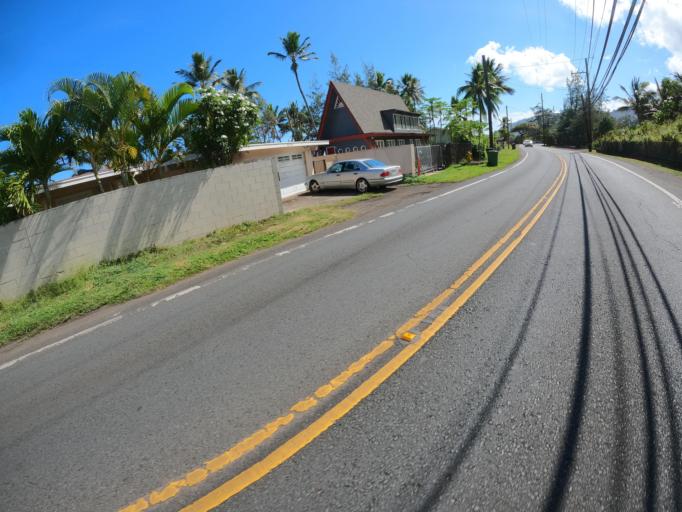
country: US
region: Hawaii
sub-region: Honolulu County
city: Hau'ula
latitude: 21.5976
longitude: -157.8969
